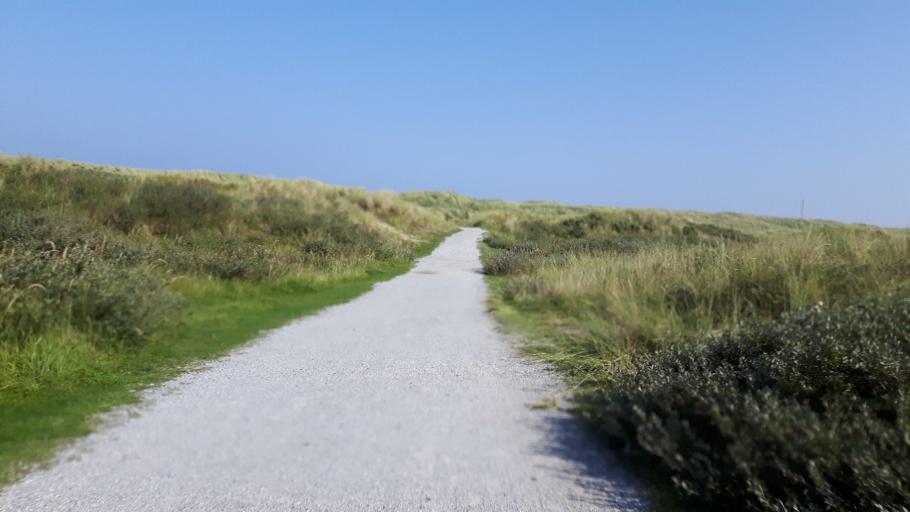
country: NL
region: Friesland
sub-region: Gemeente Ameland
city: Nes
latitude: 53.4599
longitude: 5.8163
